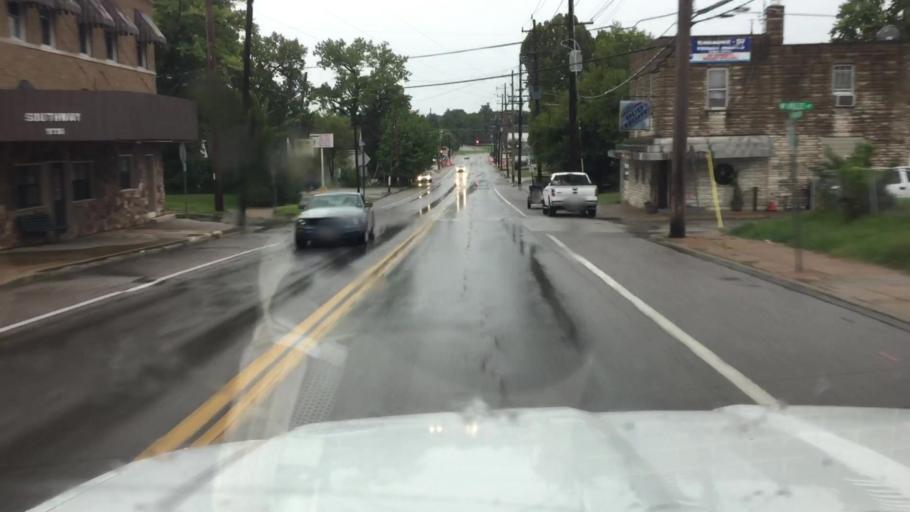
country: US
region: Missouri
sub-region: Saint Louis County
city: Lemay
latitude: 38.5269
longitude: -90.2773
